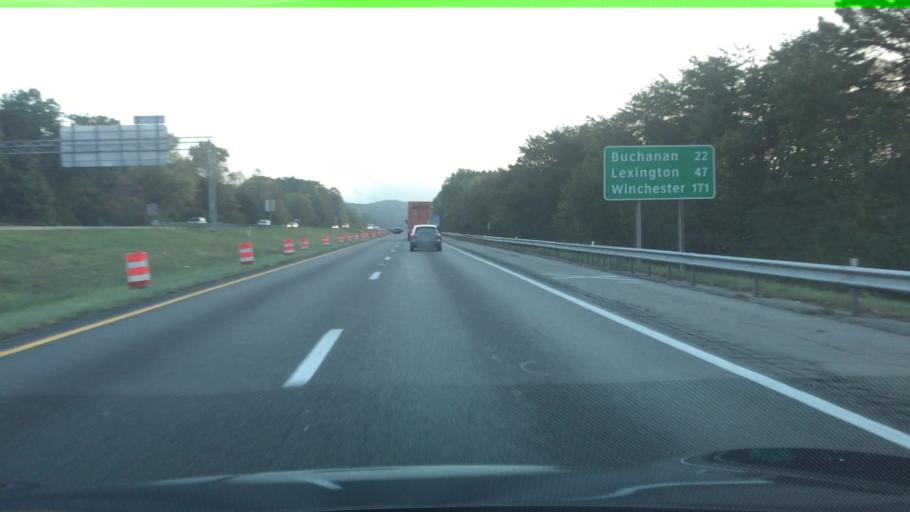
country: US
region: Virginia
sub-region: Roanoke County
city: Hollins
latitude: 37.3492
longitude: -79.9863
